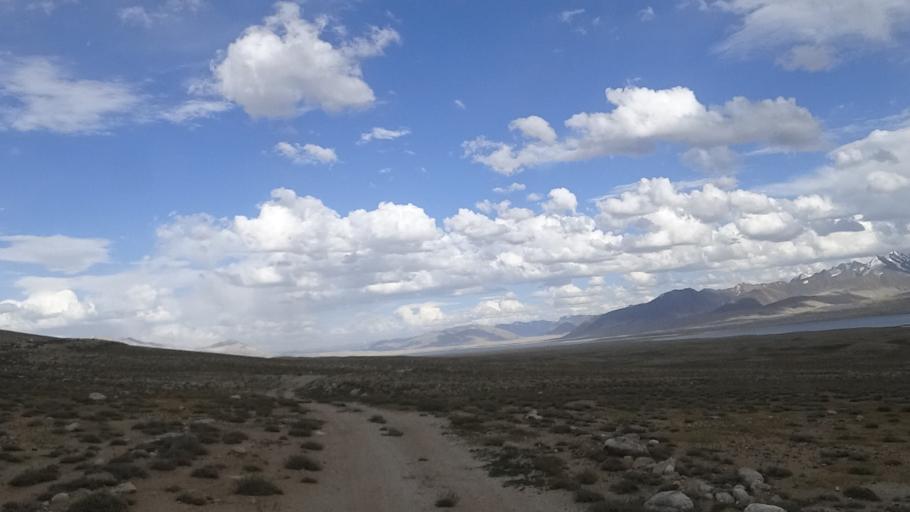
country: TJ
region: Gorno-Badakhshan
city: Murghob
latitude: 37.4683
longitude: 73.5815
